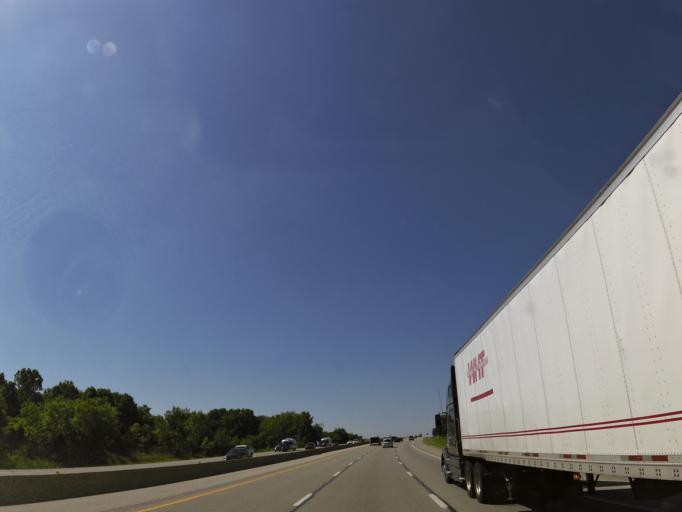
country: US
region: Kentucky
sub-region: Madison County
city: Berea
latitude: 37.6185
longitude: -84.3143
